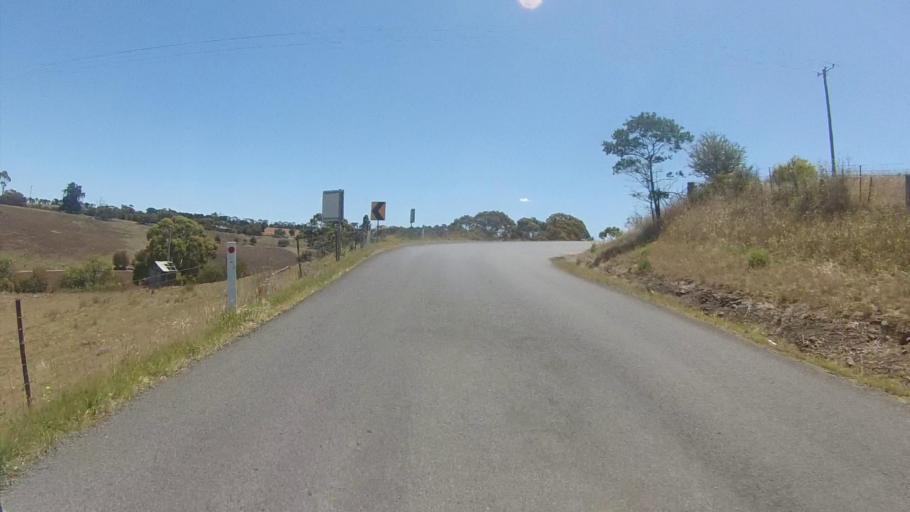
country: AU
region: Tasmania
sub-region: Sorell
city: Sorell
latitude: -42.7708
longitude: 147.5947
